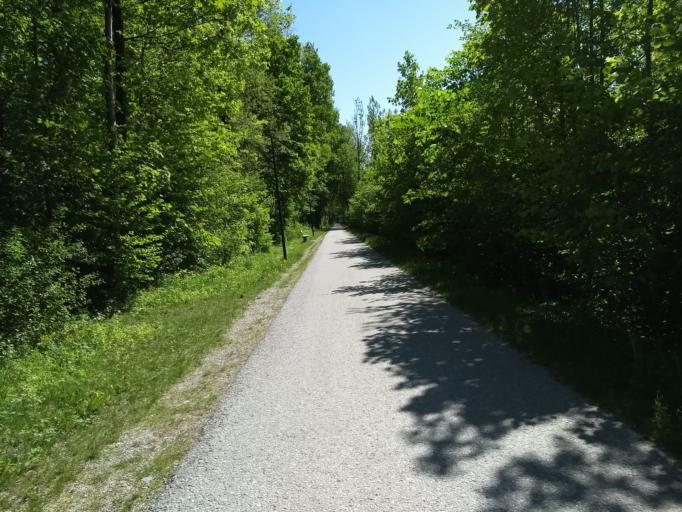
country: AT
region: Salzburg
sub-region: Politischer Bezirk Salzburg-Umgebung
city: Elsbethen
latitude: 47.7758
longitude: 13.0763
